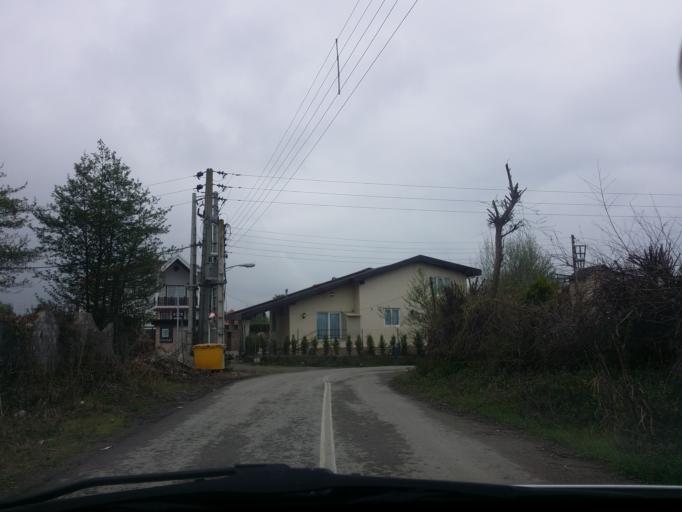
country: IR
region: Mazandaran
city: Chalus
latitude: 36.6767
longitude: 51.3787
